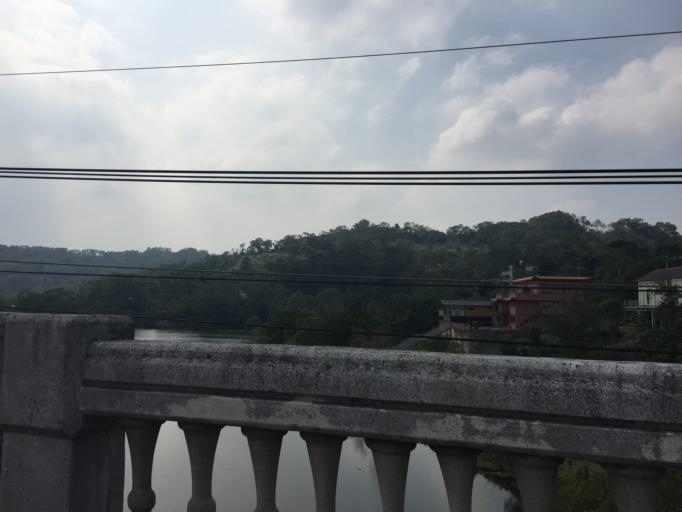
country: TW
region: Taiwan
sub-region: Hsinchu
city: Hsinchu
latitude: 24.6818
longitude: 120.9822
